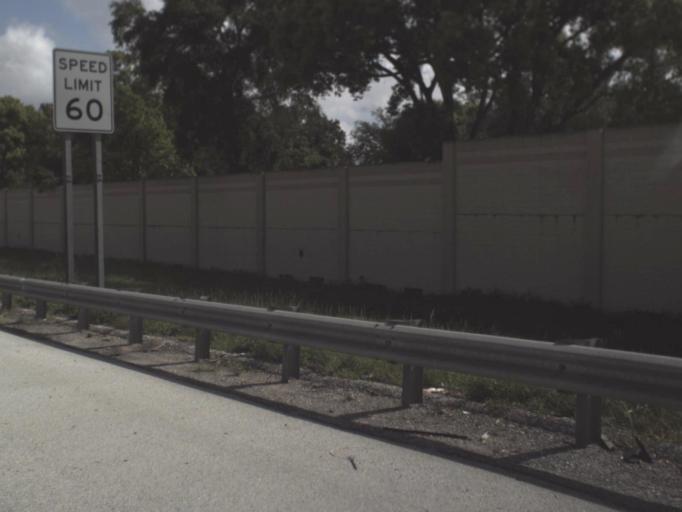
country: US
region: Florida
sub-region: Hillsborough County
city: University
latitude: 28.0639
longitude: -82.4546
